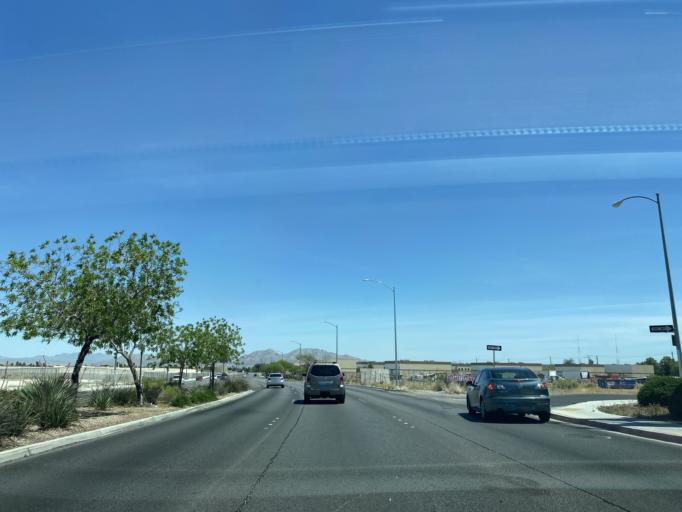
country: US
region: Nevada
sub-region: Clark County
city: Las Vegas
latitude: 36.1976
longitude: -115.1884
